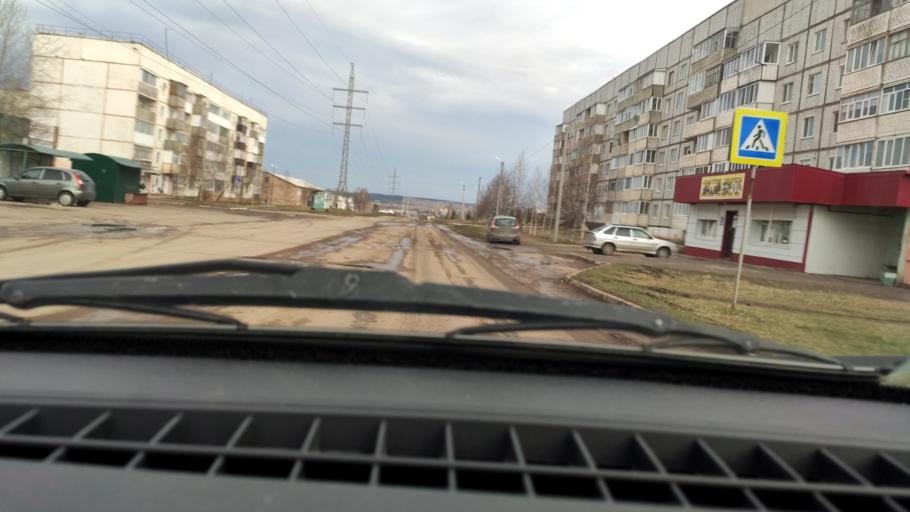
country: RU
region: Bashkortostan
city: Davlekanovo
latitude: 54.2281
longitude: 55.0354
